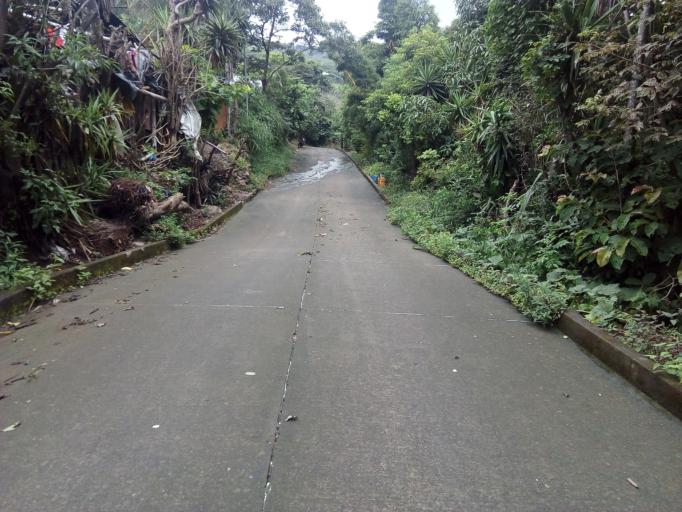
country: GT
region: Escuintla
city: Guanagazapa
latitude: 14.3136
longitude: -90.5595
